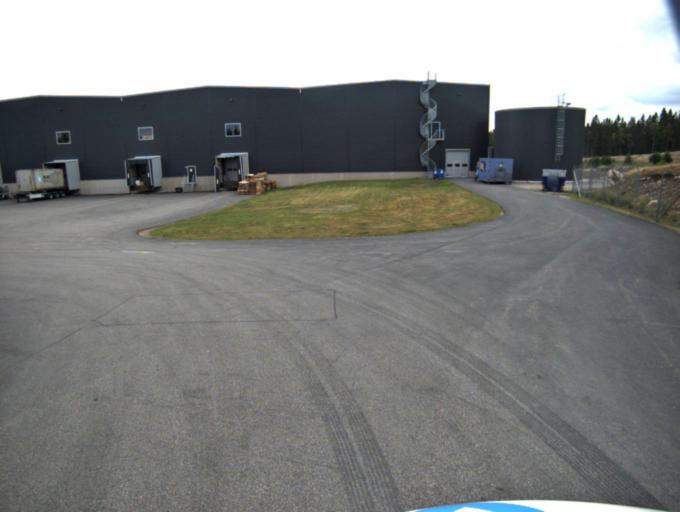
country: SE
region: Vaestra Goetaland
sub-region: Ulricehamns Kommun
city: Ulricehamn
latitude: 57.8020
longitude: 13.4669
